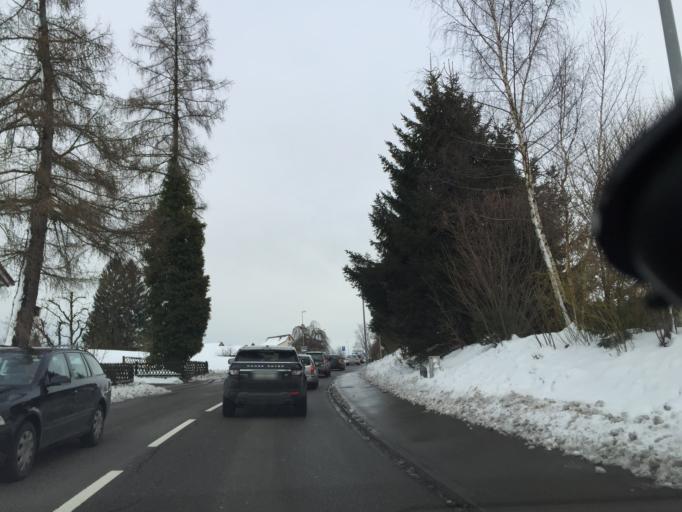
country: CH
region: Zurich
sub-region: Bezirk Horgen
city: Richterswil / Burghalde
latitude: 47.1984
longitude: 8.6847
